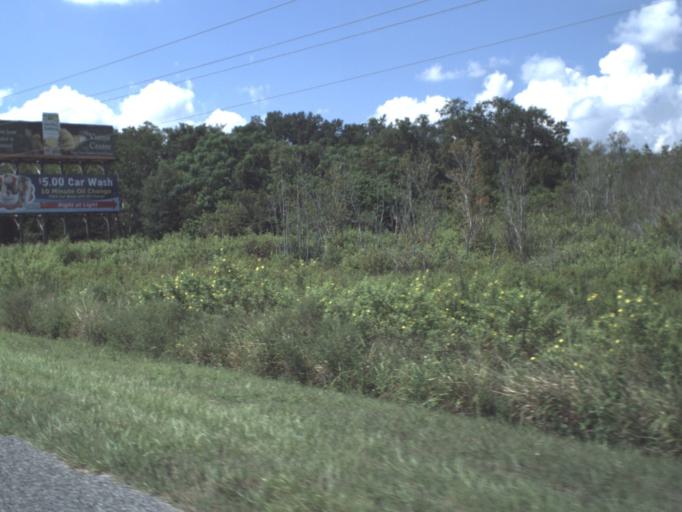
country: US
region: Florida
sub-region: Polk County
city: Haines City
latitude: 28.0872
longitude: -81.6494
